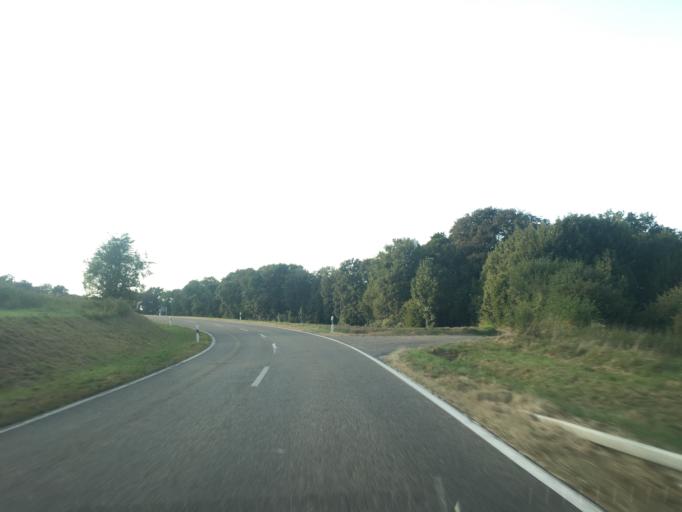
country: DE
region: Baden-Wuerttemberg
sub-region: Tuebingen Region
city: Obermarchtal
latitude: 48.2362
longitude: 9.5654
